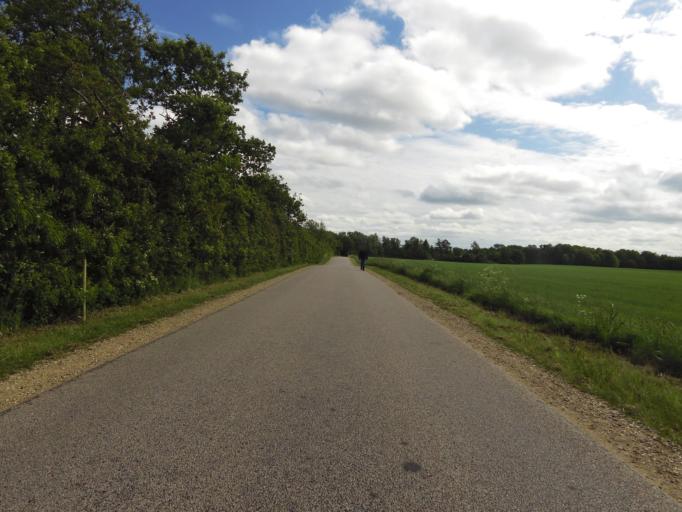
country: DK
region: South Denmark
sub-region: Vejen Kommune
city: Vejen
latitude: 55.4394
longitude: 9.1101
